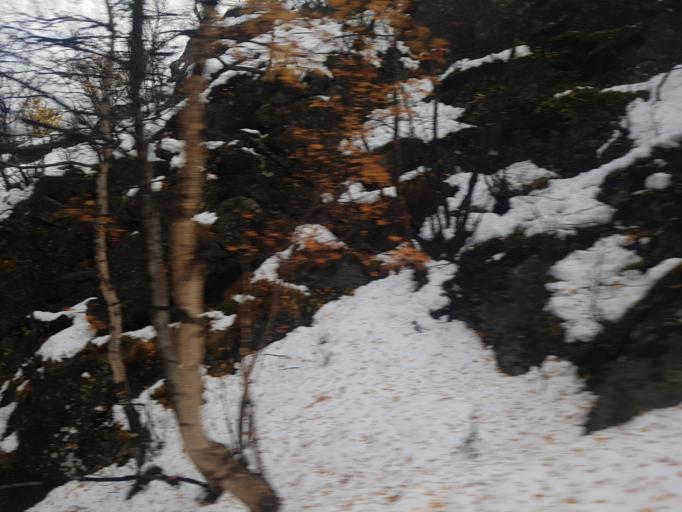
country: NO
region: Sor-Trondelag
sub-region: Oppdal
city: Oppdal
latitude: 62.3465
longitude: 9.6262
